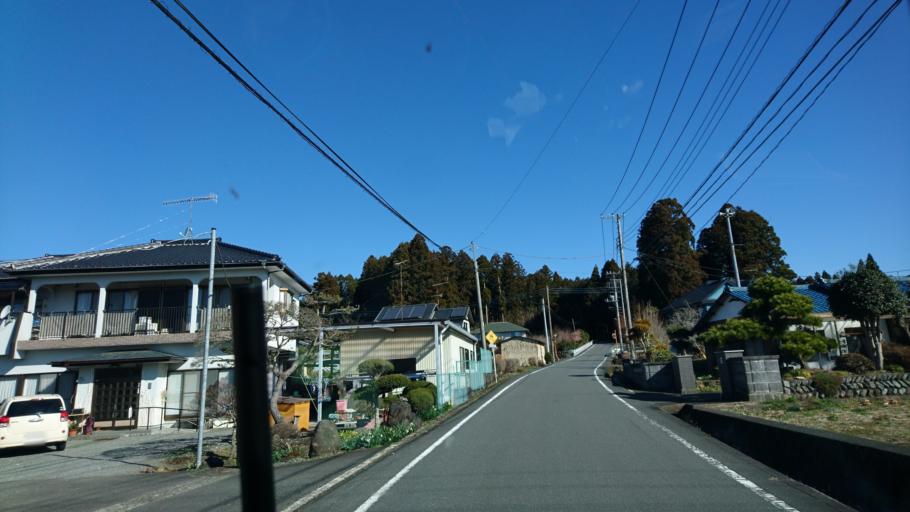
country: JP
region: Shizuoka
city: Fujinomiya
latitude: 35.3294
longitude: 138.5752
